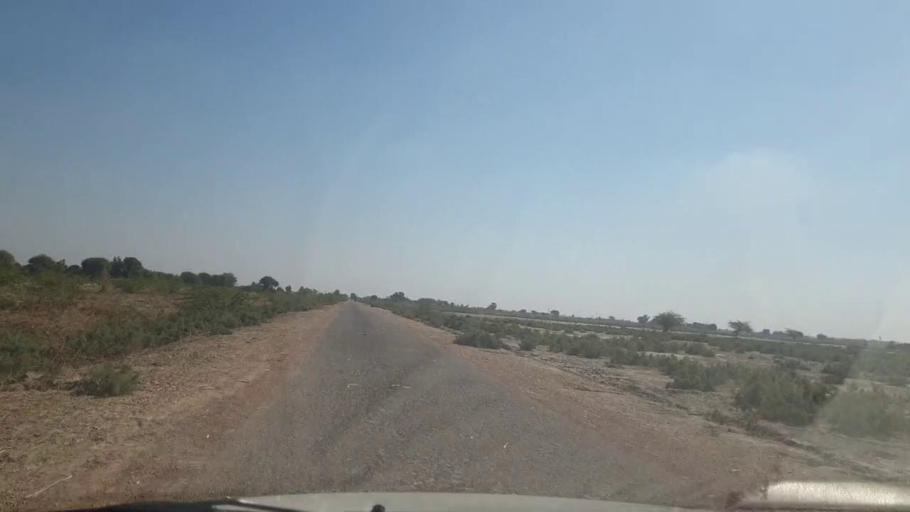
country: PK
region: Sindh
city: Mirpur Khas
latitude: 25.4938
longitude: 69.1659
